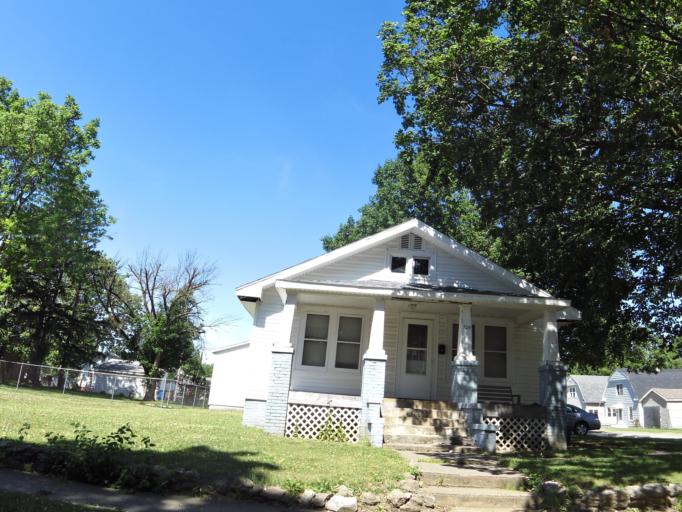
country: US
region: Illinois
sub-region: Vermilion County
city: Danville
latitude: 40.1351
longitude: -87.5982
